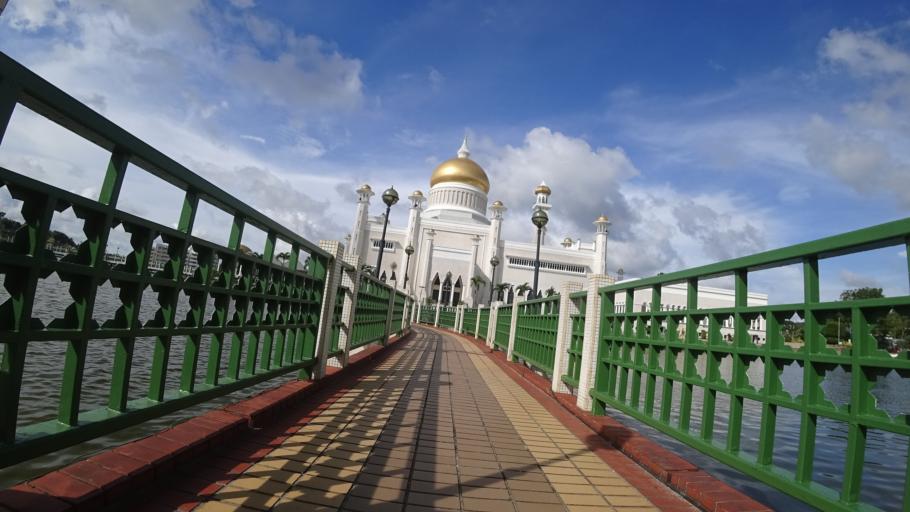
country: BN
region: Brunei and Muara
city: Bandar Seri Begawan
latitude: 4.8887
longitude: 114.9390
